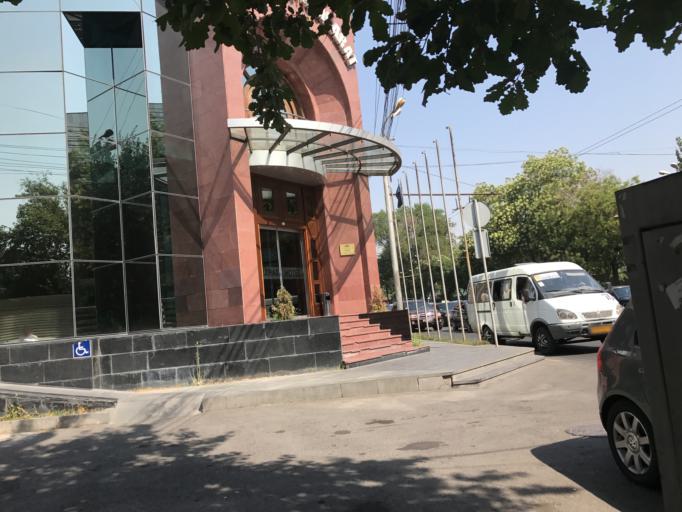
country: AM
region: Yerevan
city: Yerevan
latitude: 40.1731
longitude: 44.5067
